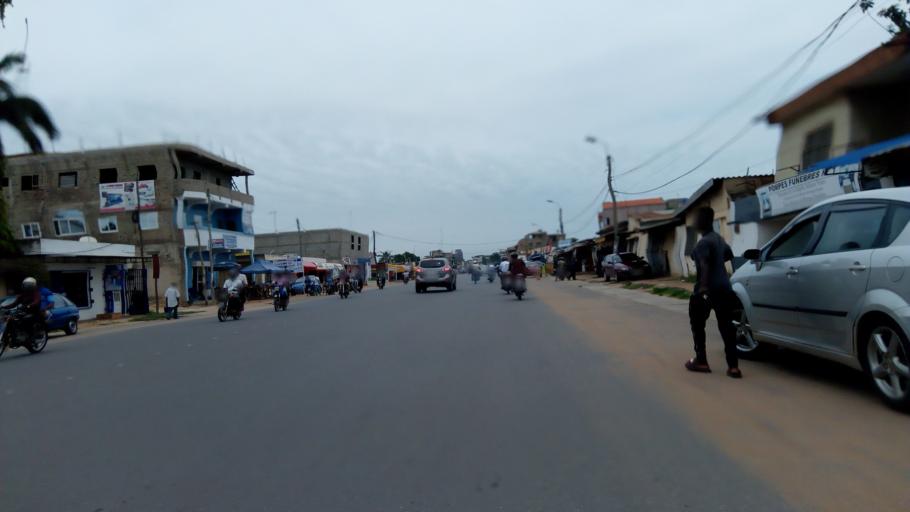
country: TG
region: Maritime
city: Lome
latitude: 6.1579
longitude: 1.2334
